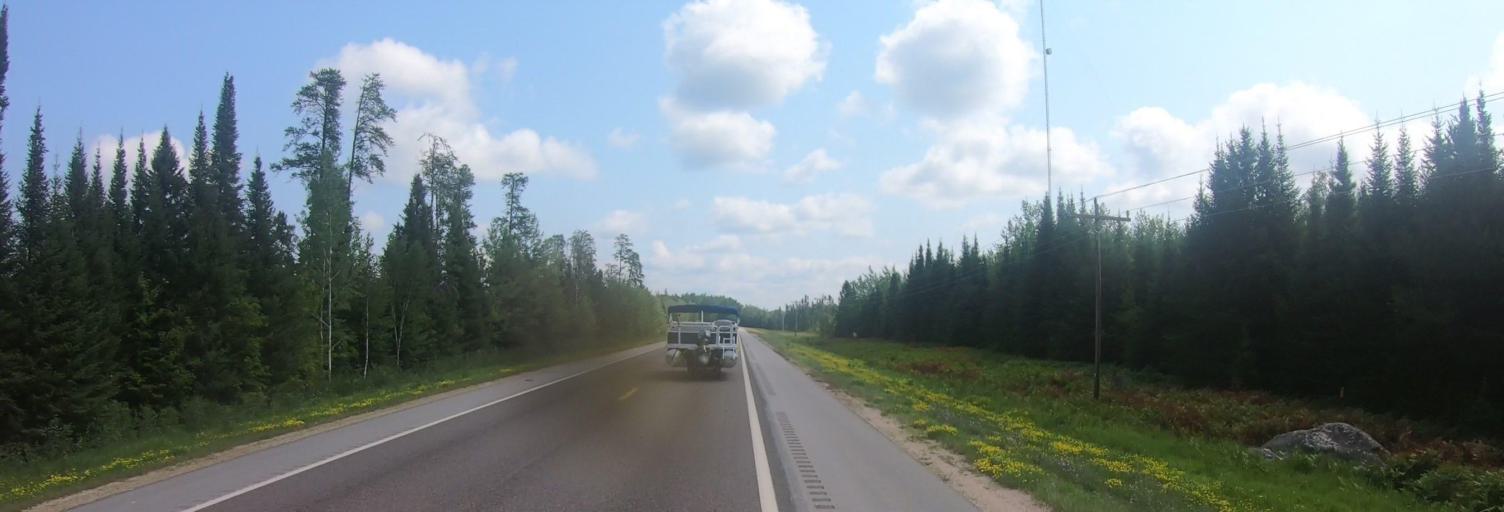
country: US
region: Minnesota
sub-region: Saint Louis County
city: Mountain Iron
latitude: 48.0931
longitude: -92.6003
